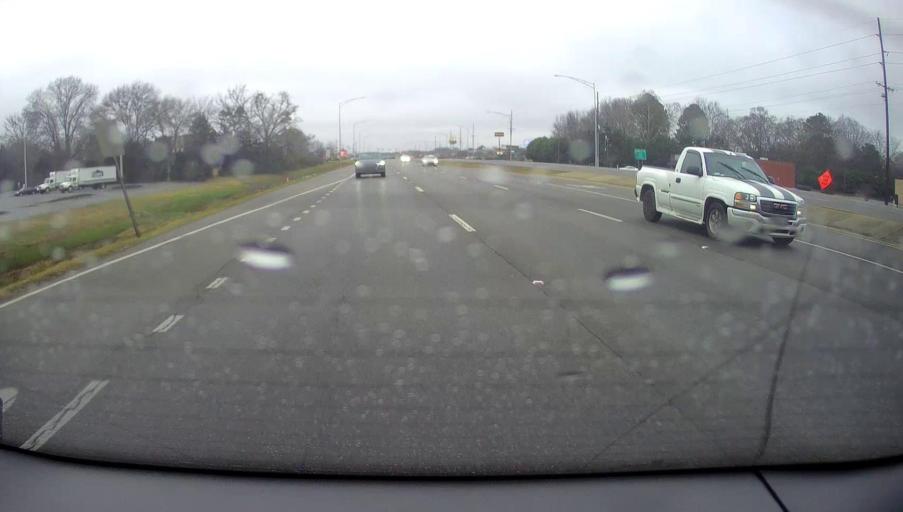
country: US
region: Alabama
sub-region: Morgan County
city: Decatur
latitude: 34.5681
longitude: -87.0123
